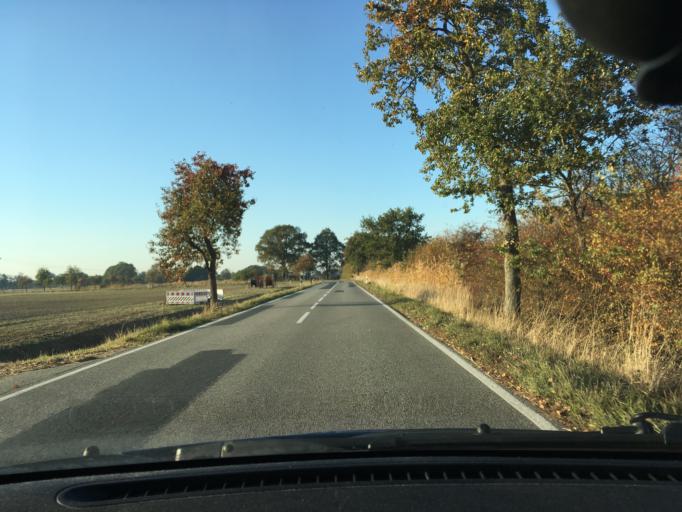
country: DE
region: Lower Saxony
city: Bleckede
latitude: 53.2961
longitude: 10.8007
